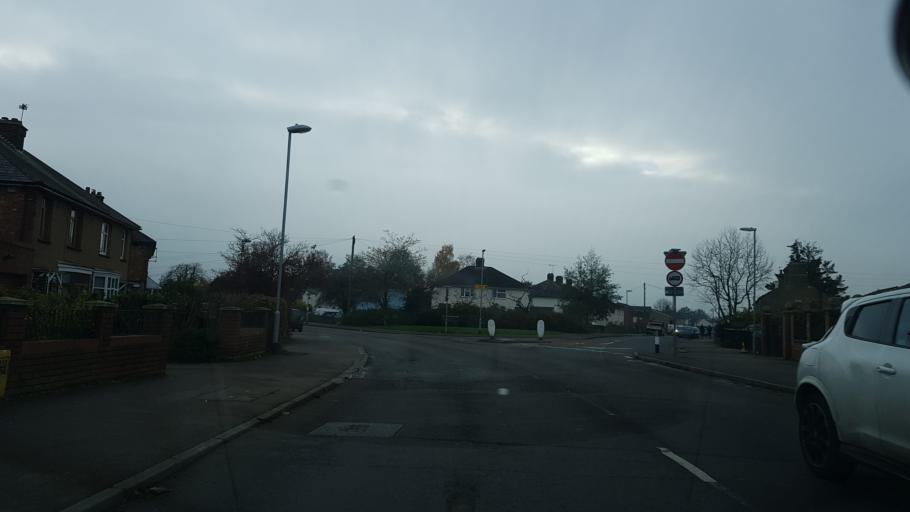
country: GB
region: England
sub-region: Central Bedfordshire
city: Biggleswade
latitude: 52.0939
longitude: -0.2540
